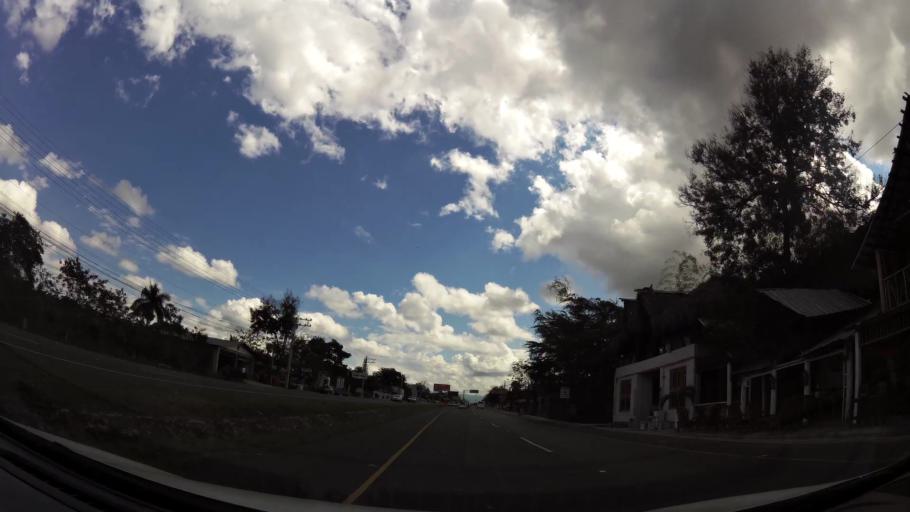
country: DO
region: La Vega
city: Rio Verde Arriba
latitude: 19.3539
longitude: -70.6009
